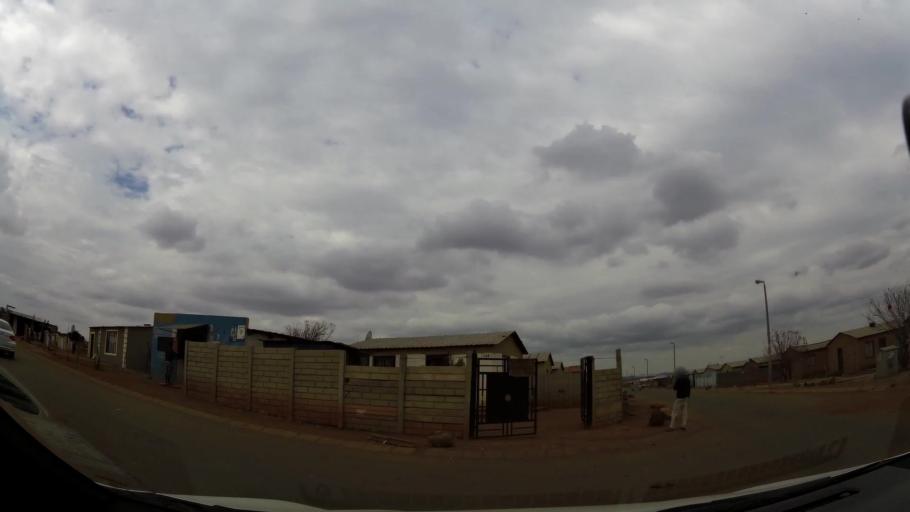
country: ZA
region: Gauteng
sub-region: Ekurhuleni Metropolitan Municipality
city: Germiston
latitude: -26.3828
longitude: 28.1176
